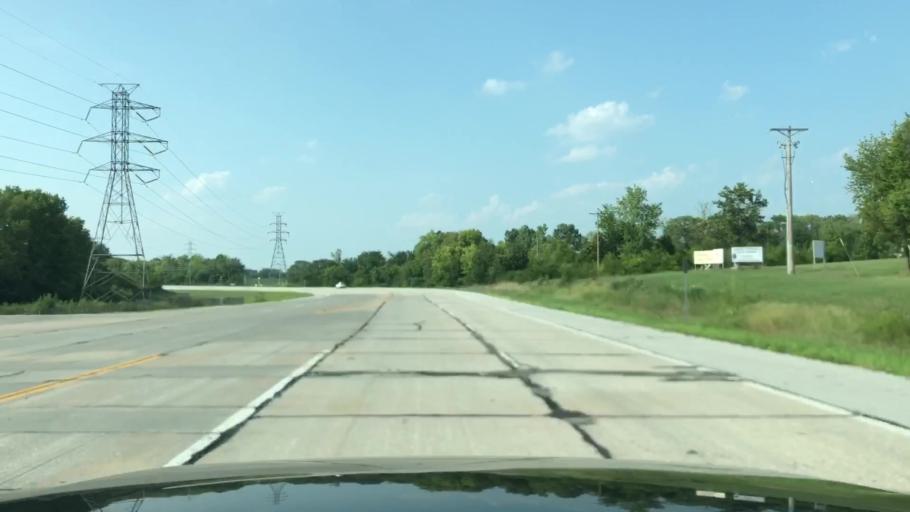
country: US
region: Missouri
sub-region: Saint Charles County
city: Lake Saint Louis
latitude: 38.8167
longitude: -90.8116
